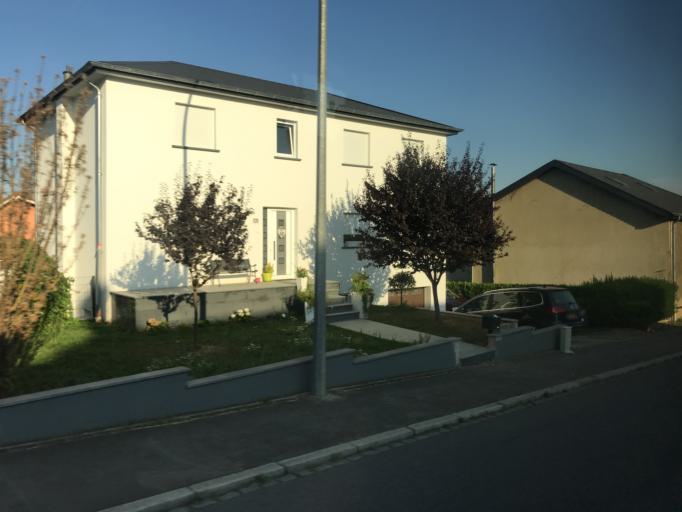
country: LU
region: Luxembourg
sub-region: Canton d'Esch-sur-Alzette
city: Frisange
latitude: 49.5223
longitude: 6.1854
